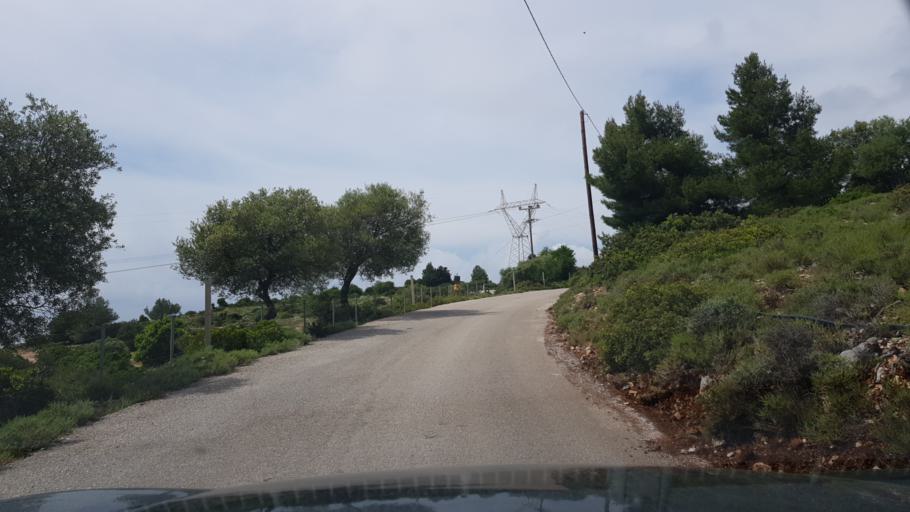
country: GR
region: Ionian Islands
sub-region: Lefkada
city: Nidri
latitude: 38.6183
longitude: 20.5654
